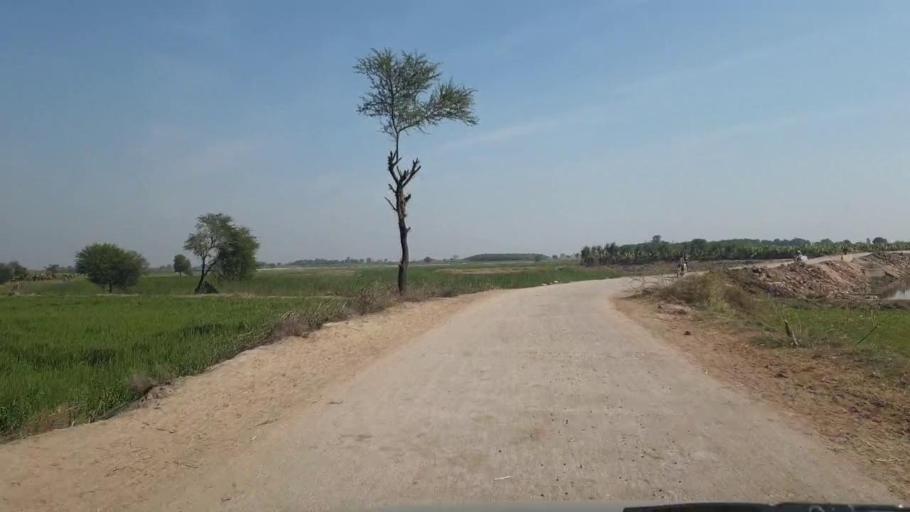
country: PK
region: Sindh
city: Chambar
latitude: 25.3864
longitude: 68.7841
